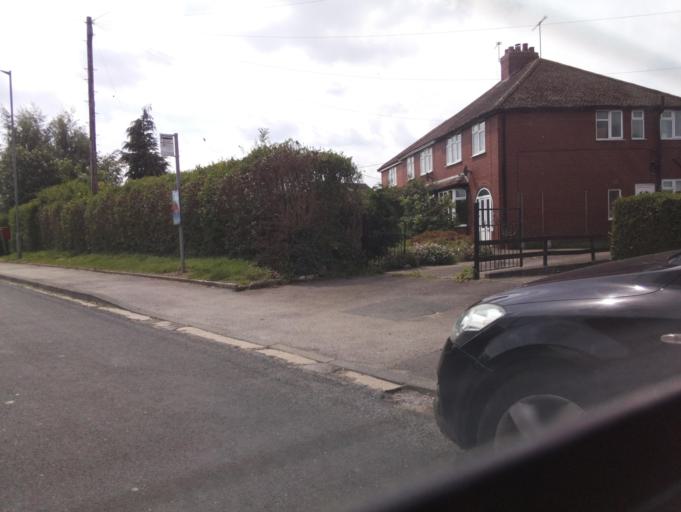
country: GB
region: England
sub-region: North Yorkshire
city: Boroughbridge
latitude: 54.0846
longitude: -1.3959
